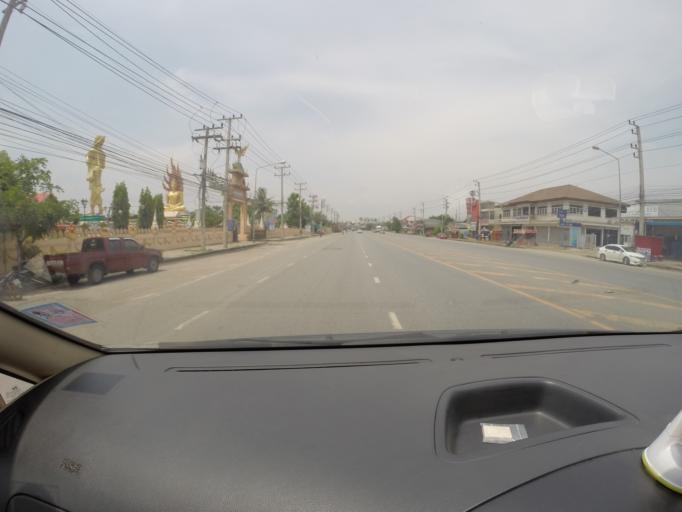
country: TH
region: Chaiyaphum
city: Noen Sa-nga
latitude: 15.6861
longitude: 102.0105
